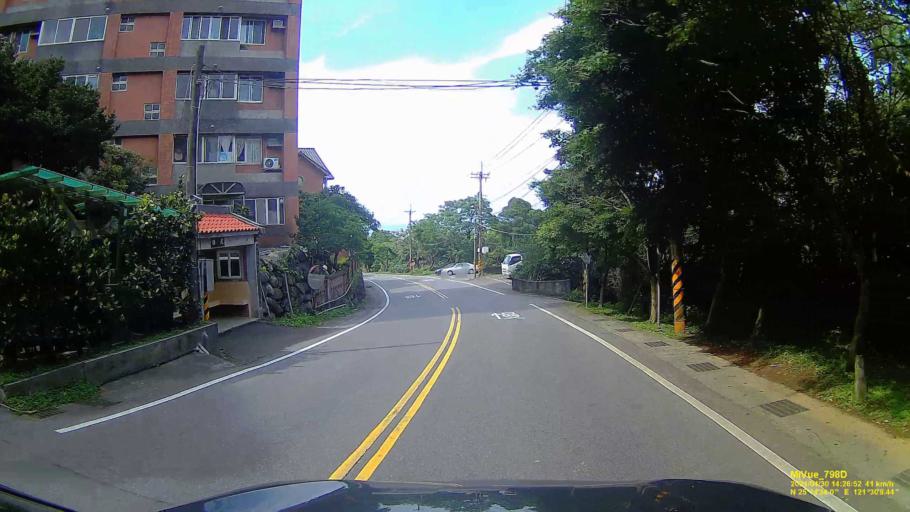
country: TW
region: Taipei
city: Taipei
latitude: 25.2431
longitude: 121.5027
